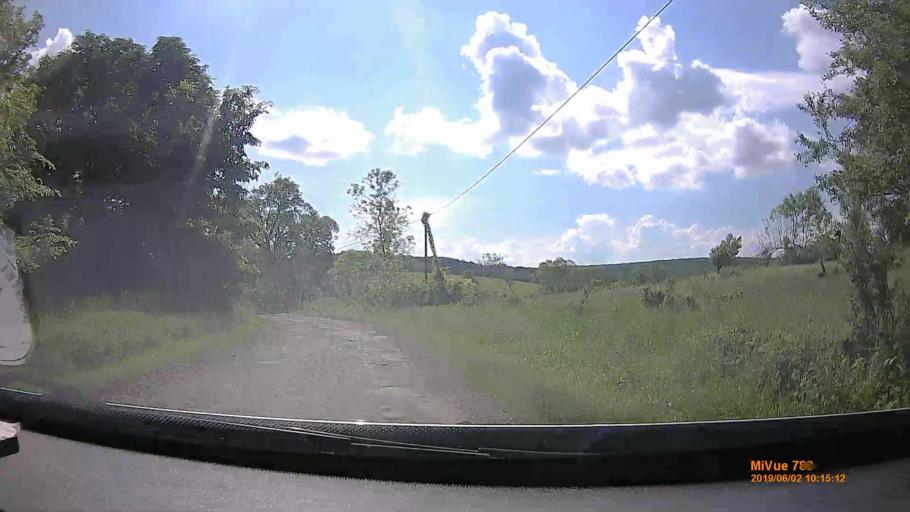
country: HU
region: Borsod-Abauj-Zemplen
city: Szendro
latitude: 48.5075
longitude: 20.7986
